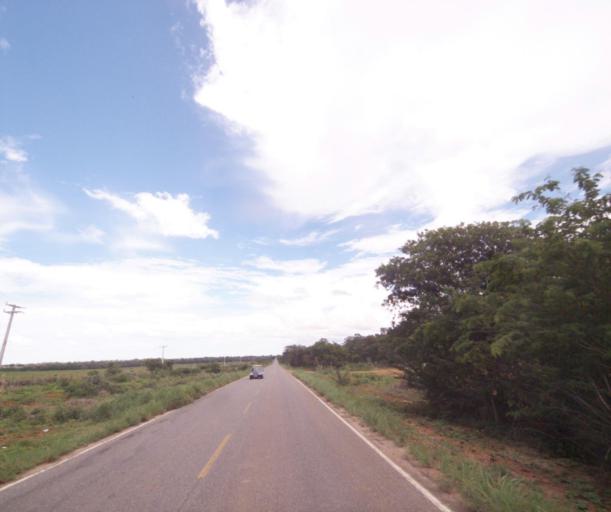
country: BR
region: Bahia
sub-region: Carinhanha
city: Carinhanha
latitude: -14.2867
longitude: -43.6097
